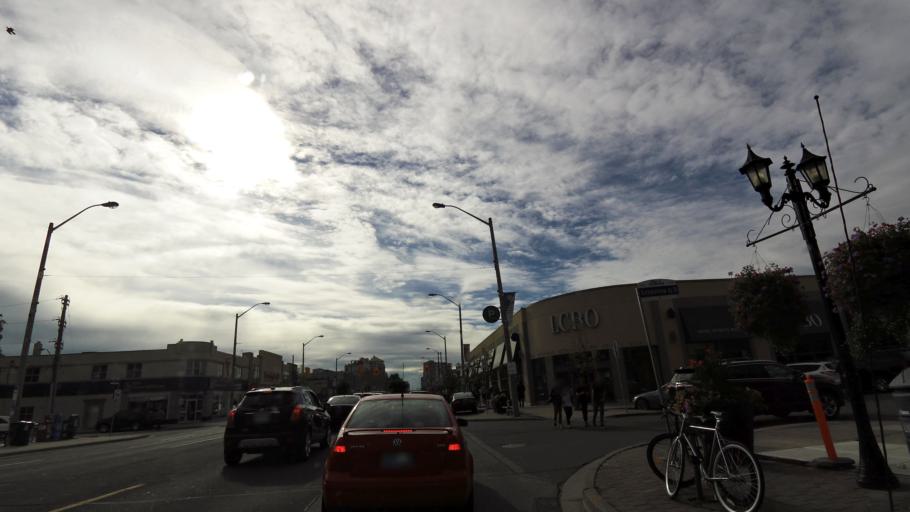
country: CA
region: Ontario
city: Etobicoke
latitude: 43.6483
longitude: -79.5076
